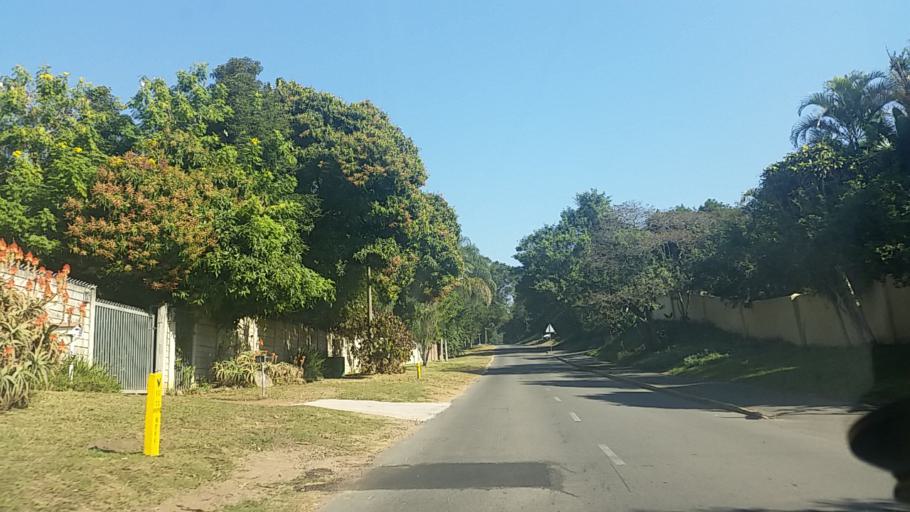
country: ZA
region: KwaZulu-Natal
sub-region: eThekwini Metropolitan Municipality
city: Berea
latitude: -29.8477
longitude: 30.9043
